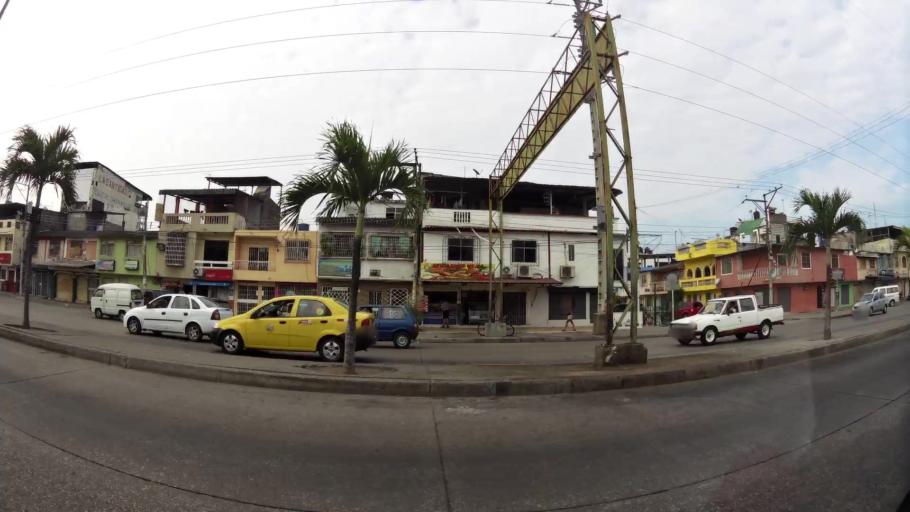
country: EC
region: Guayas
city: Guayaquil
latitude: -2.2510
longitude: -79.8910
